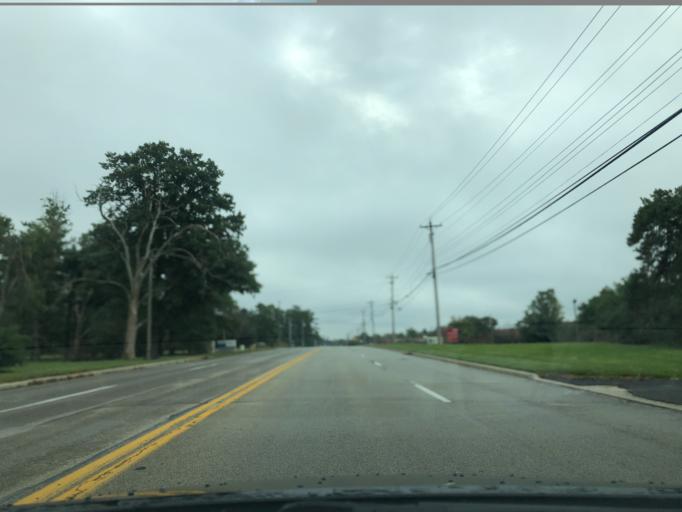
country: US
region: Ohio
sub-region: Hamilton County
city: Highpoint
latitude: 39.2805
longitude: -84.3544
